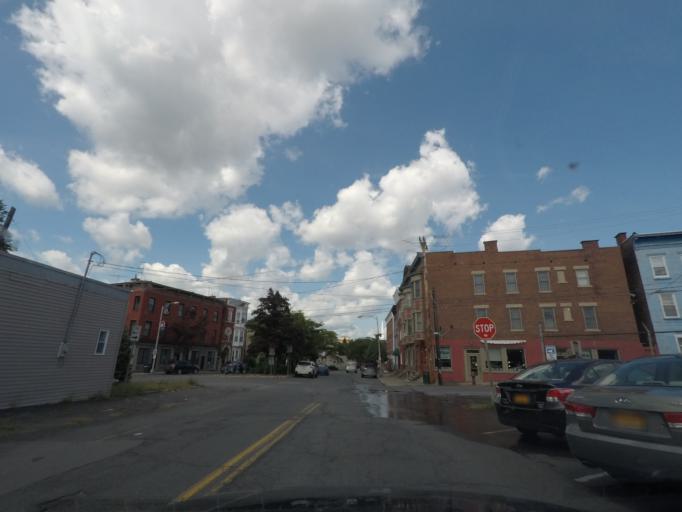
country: US
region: New York
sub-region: Rensselaer County
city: Troy
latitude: 42.7250
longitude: -73.6900
